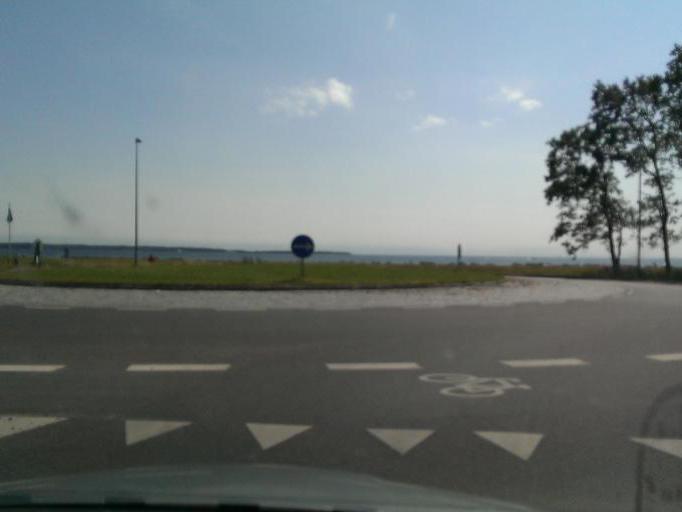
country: DK
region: Central Jutland
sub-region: Syddjurs Kommune
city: Ebeltoft
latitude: 56.2292
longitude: 10.6055
